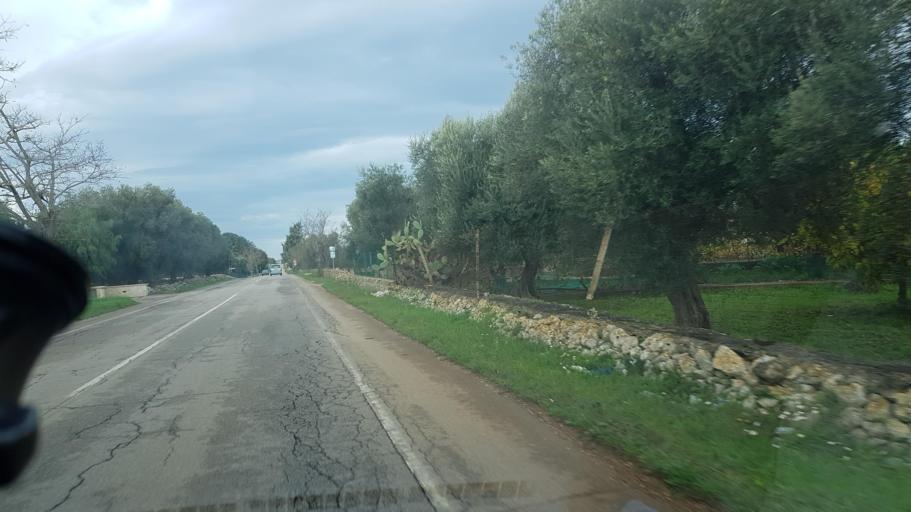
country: IT
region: Apulia
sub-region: Provincia di Brindisi
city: Carovigno
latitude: 40.6815
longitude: 17.6830
